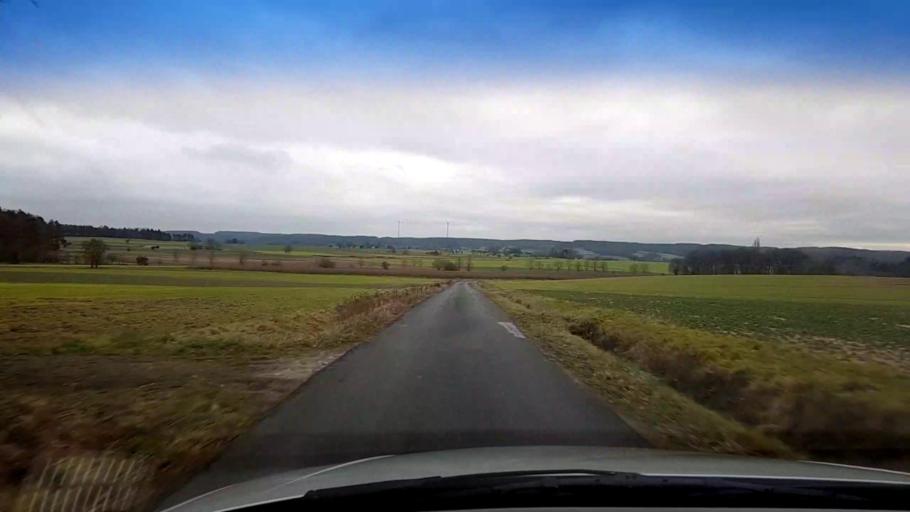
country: DE
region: Bavaria
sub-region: Upper Franconia
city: Lauter
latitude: 49.9563
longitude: 10.7781
